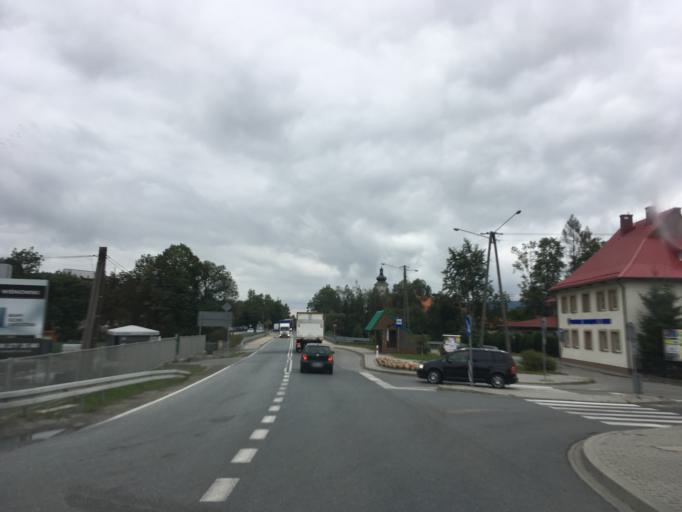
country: PL
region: Lesser Poland Voivodeship
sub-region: Powiat suski
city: Osielec
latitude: 49.6705
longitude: 19.7681
